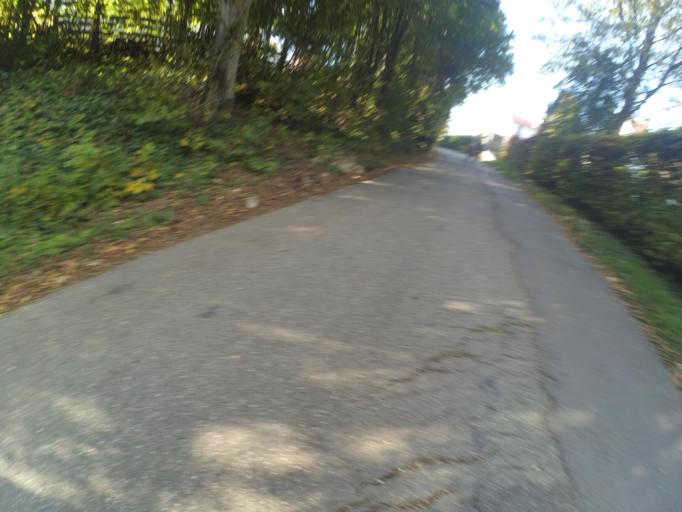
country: DE
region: Baden-Wuerttemberg
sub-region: Regierungsbezirk Stuttgart
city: Heubach
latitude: 48.7853
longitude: 9.9284
